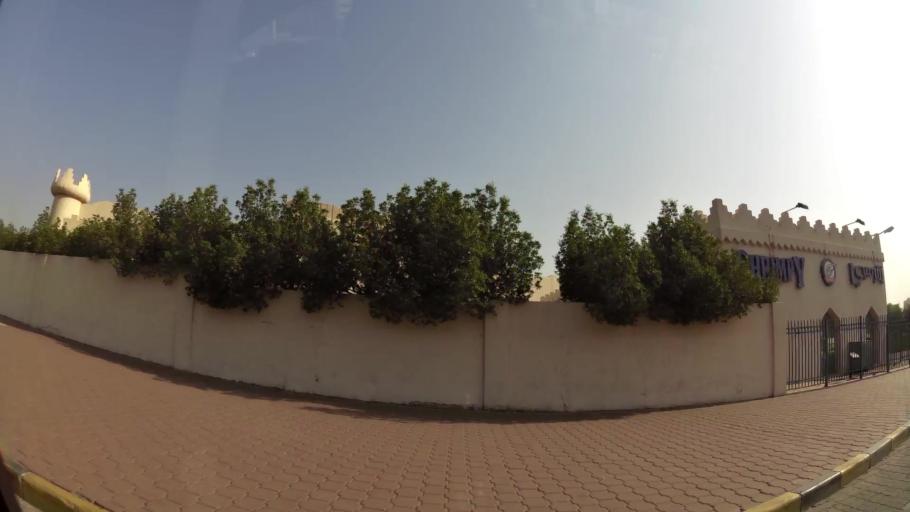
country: KW
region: Muhafazat Hawalli
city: Hawalli
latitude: 29.3393
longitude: 48.0222
